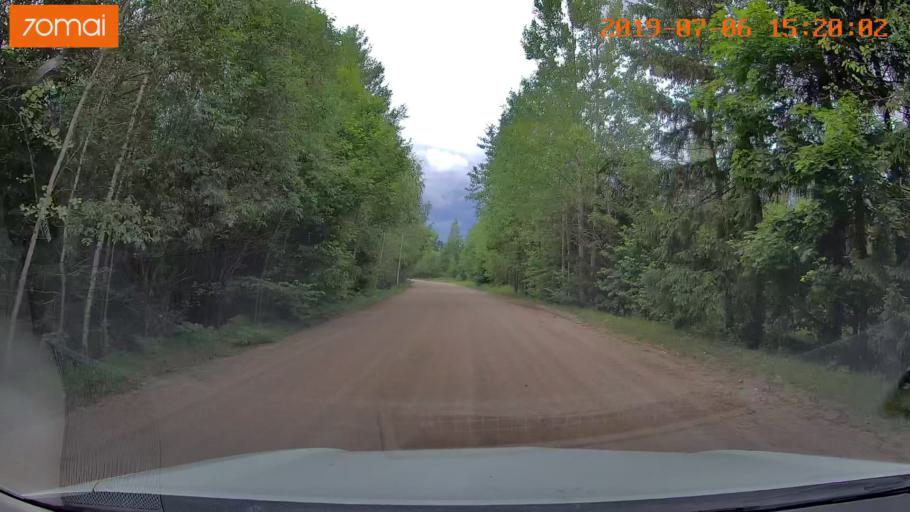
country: BY
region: Minsk
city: Valozhyn
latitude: 54.0035
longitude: 26.6418
